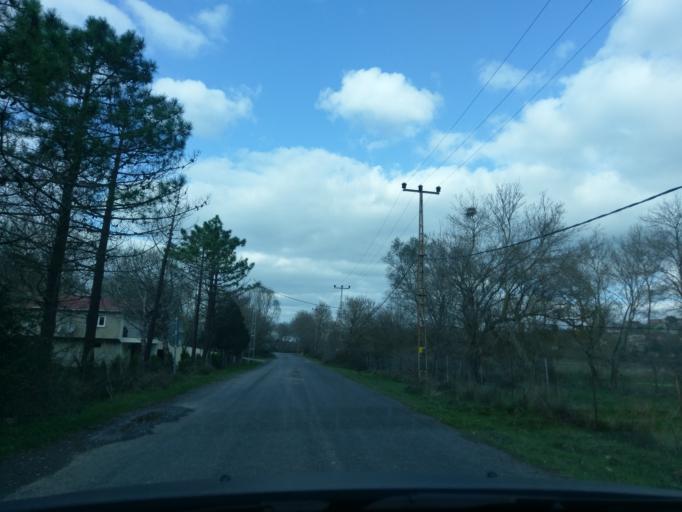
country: TR
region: Istanbul
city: Durusu
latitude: 41.2956
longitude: 28.6777
